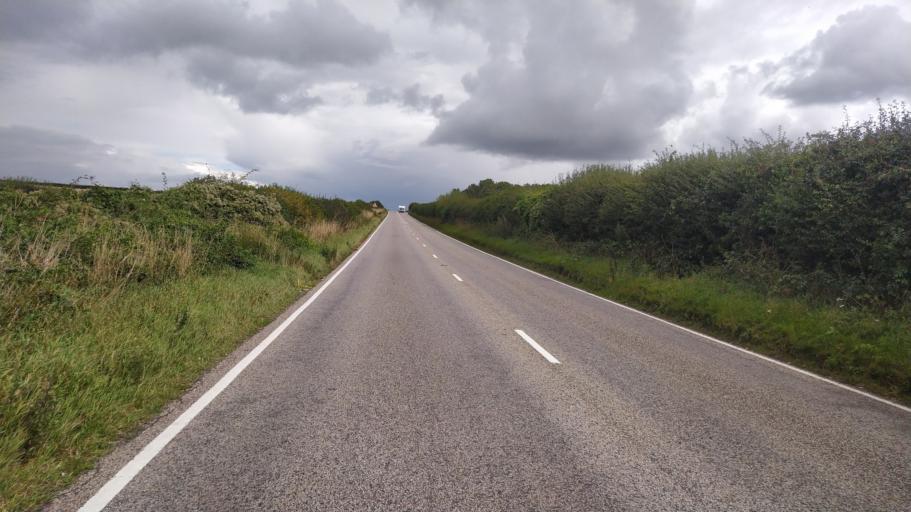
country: GB
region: England
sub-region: Dorset
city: Blandford Forum
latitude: 50.8888
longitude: -2.1208
